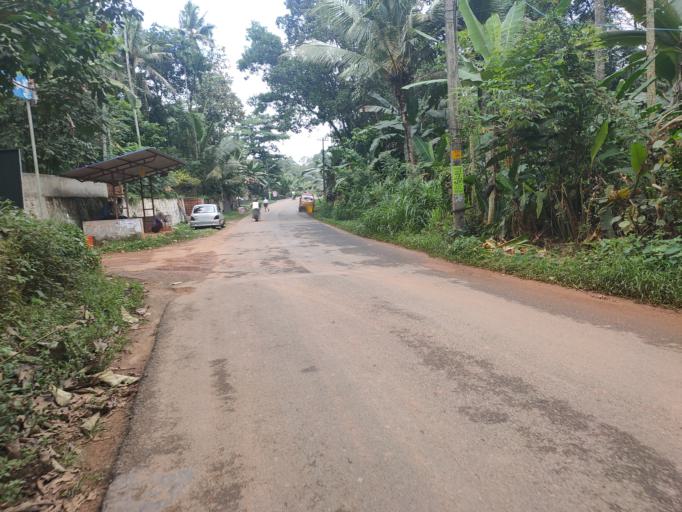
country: IN
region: Kerala
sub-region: Ernakulam
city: Muvattupula
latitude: 9.9883
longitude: 76.6367
